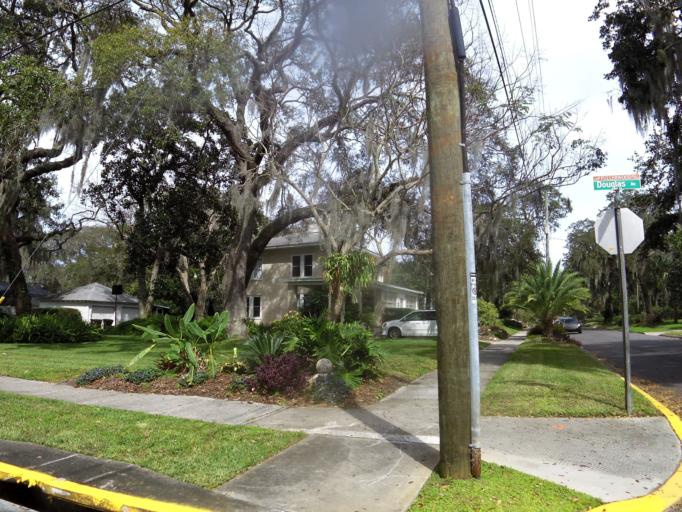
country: US
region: Florida
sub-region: Saint Johns County
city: Saint Augustine
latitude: 29.9159
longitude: -81.3205
